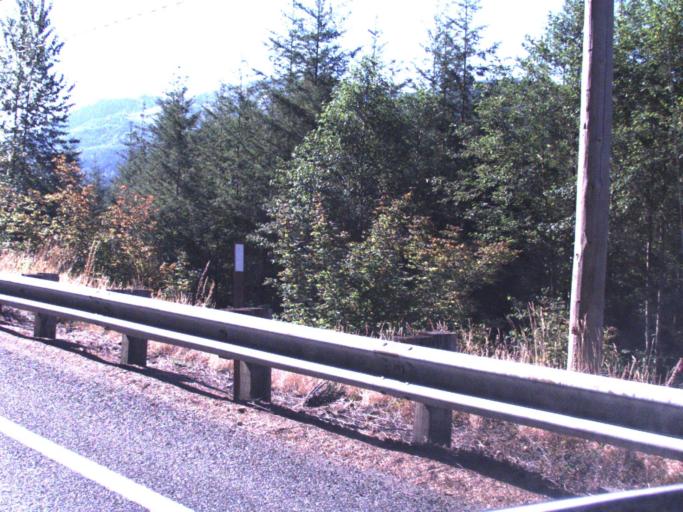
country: US
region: Washington
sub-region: King County
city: Enumclaw
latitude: 47.1529
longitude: -121.8517
